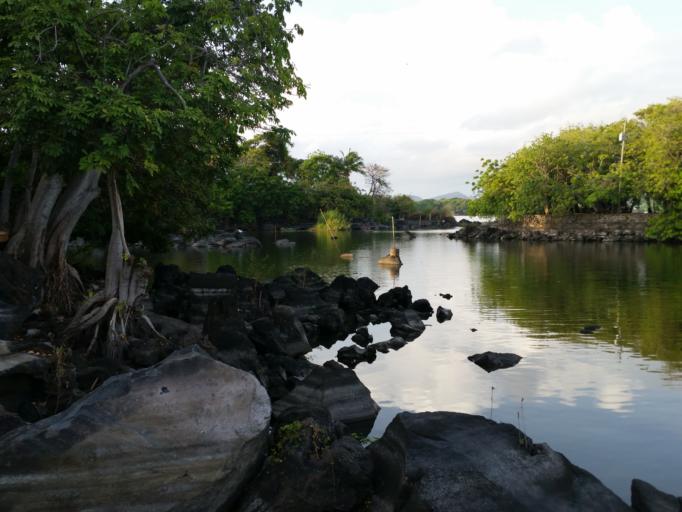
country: NI
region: Granada
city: Granada
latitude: 11.8862
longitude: -85.9021
